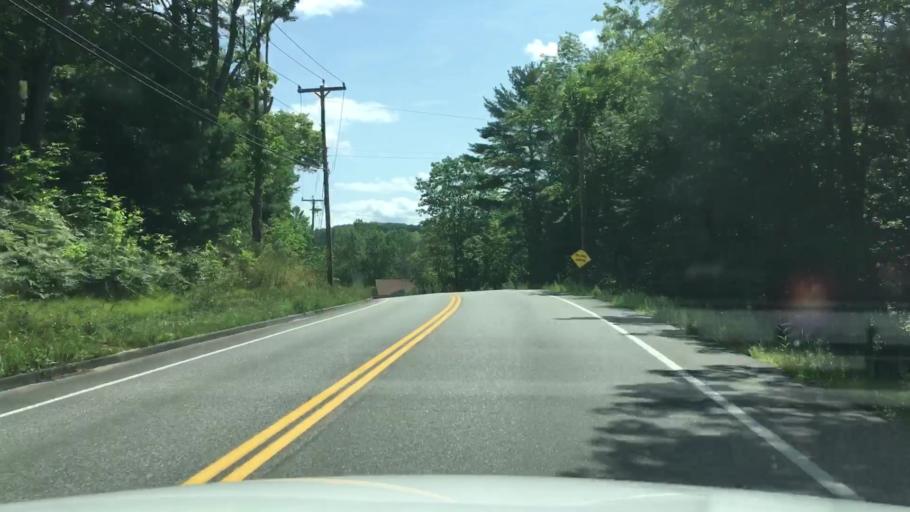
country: US
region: Maine
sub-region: Kennebec County
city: Augusta
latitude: 44.3350
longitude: -69.8023
